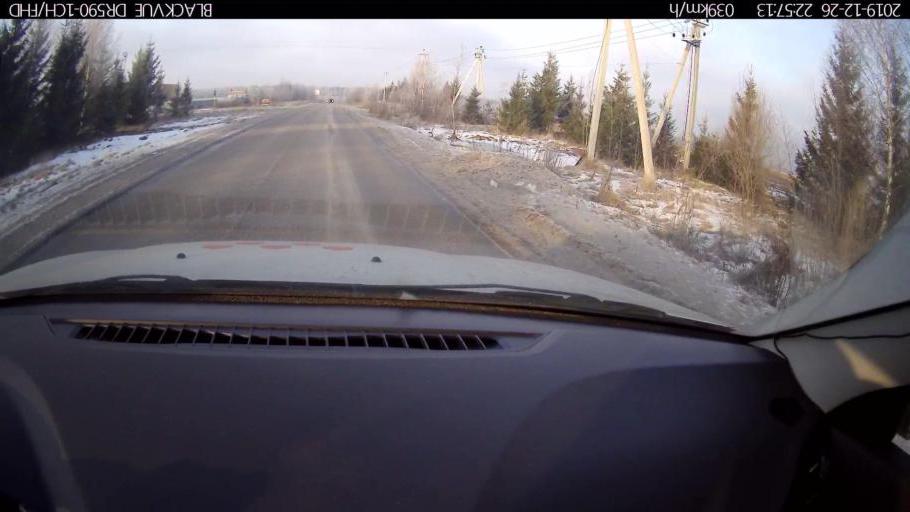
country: RU
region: Nizjnij Novgorod
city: Burevestnik
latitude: 56.1493
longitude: 43.7173
